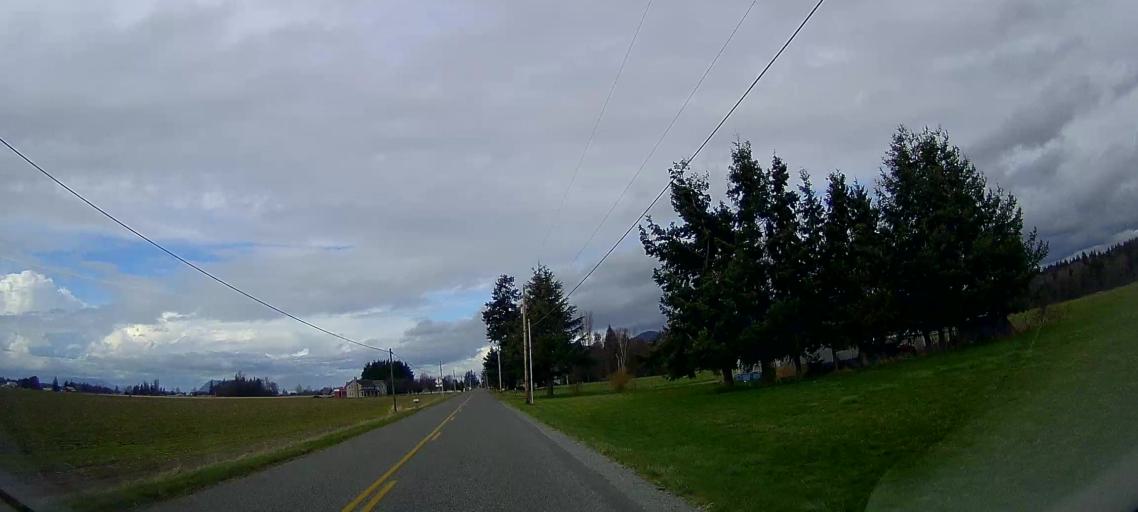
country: US
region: Washington
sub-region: Skagit County
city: Burlington
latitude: 48.5457
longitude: -122.3942
